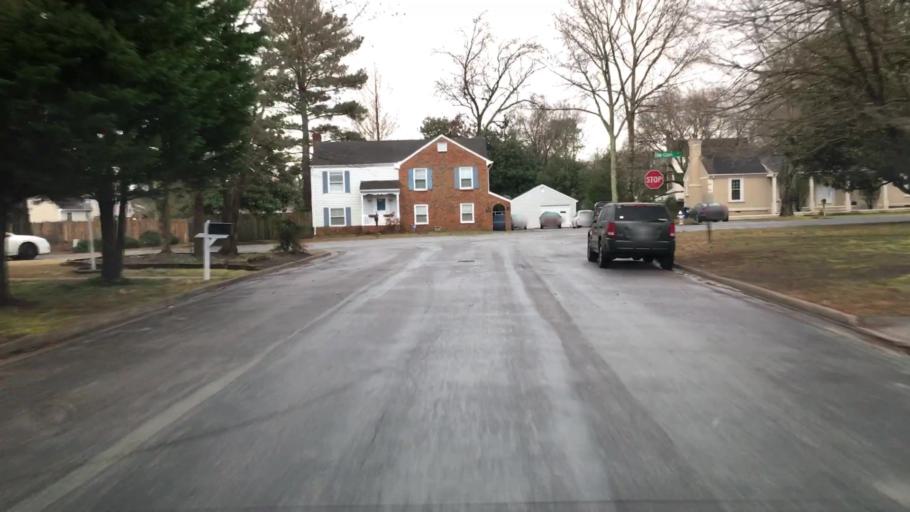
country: US
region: Virginia
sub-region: Chesterfield County
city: Bon Air
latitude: 37.5131
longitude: -77.6205
